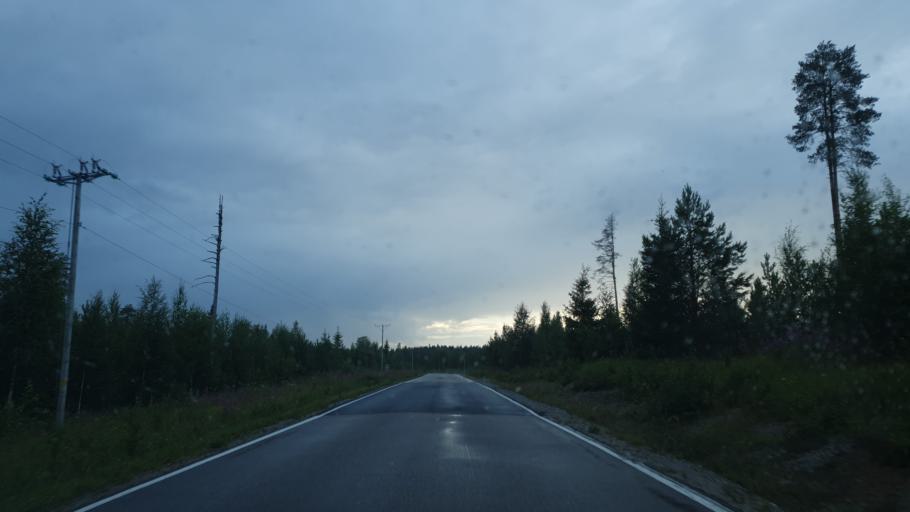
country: FI
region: North Karelia
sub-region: Pielisen Karjala
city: Lieksa
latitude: 63.6010
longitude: 29.8779
